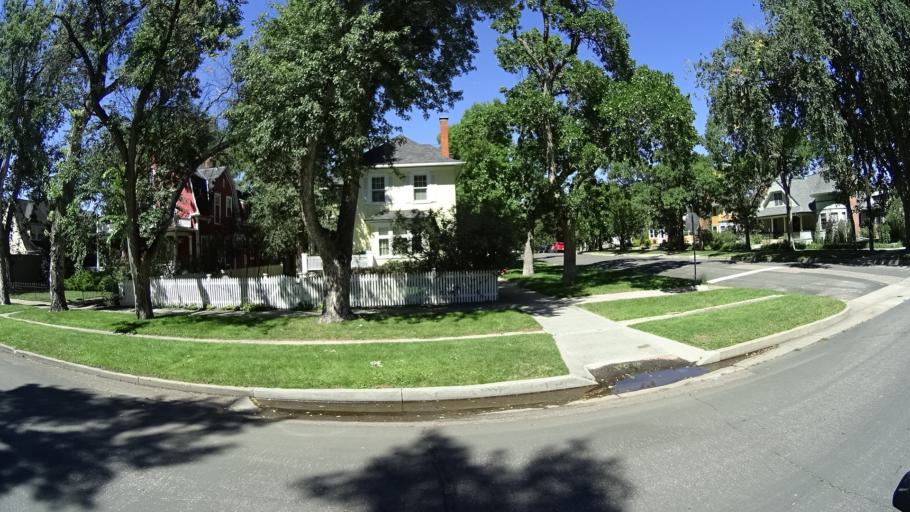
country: US
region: Colorado
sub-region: El Paso County
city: Colorado Springs
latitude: 38.8578
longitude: -104.8259
